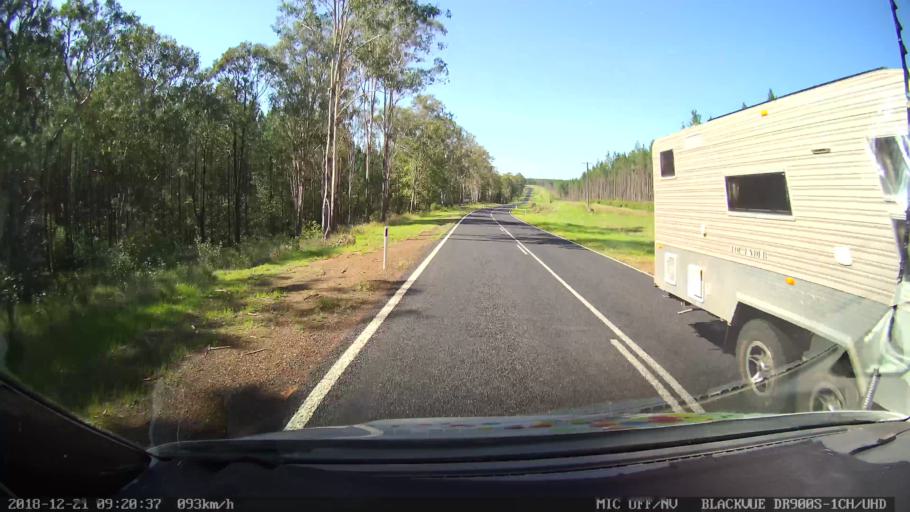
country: AU
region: New South Wales
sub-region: Clarence Valley
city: Maclean
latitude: -29.3172
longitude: 153.0002
